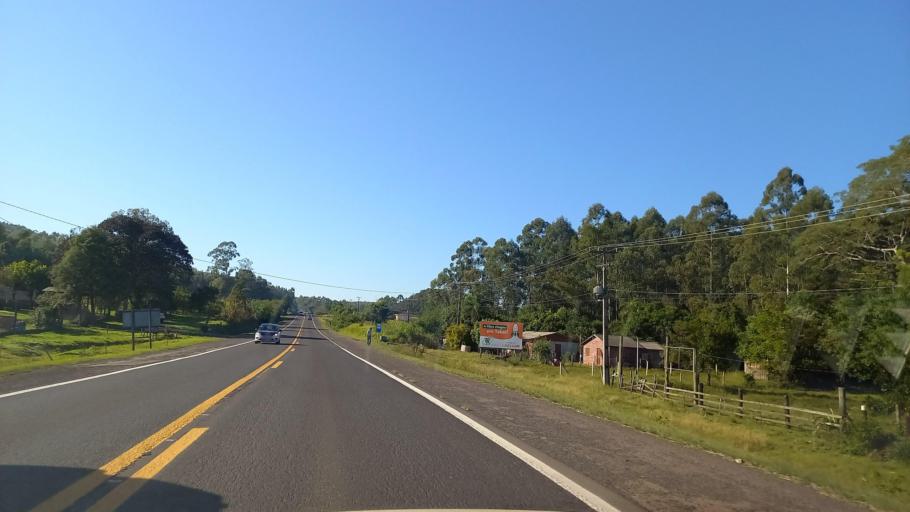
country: BR
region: Rio Grande do Sul
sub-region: Taquari
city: Taquari
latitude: -29.7081
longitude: -51.7852
